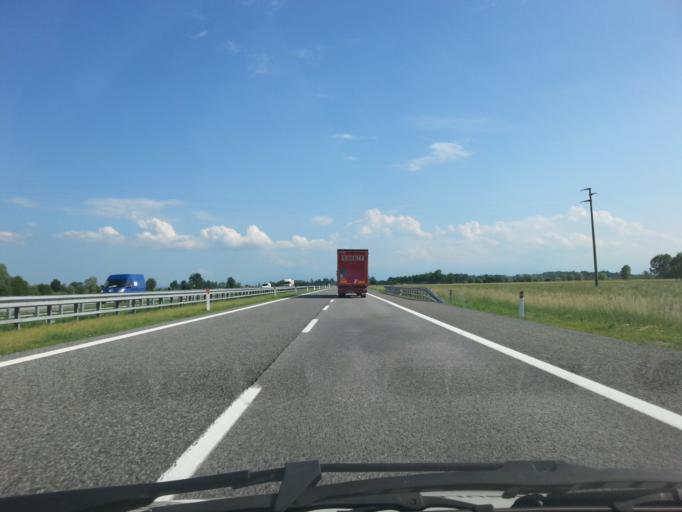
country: IT
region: Piedmont
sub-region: Provincia di Cuneo
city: Marene
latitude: 44.6884
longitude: 7.7675
